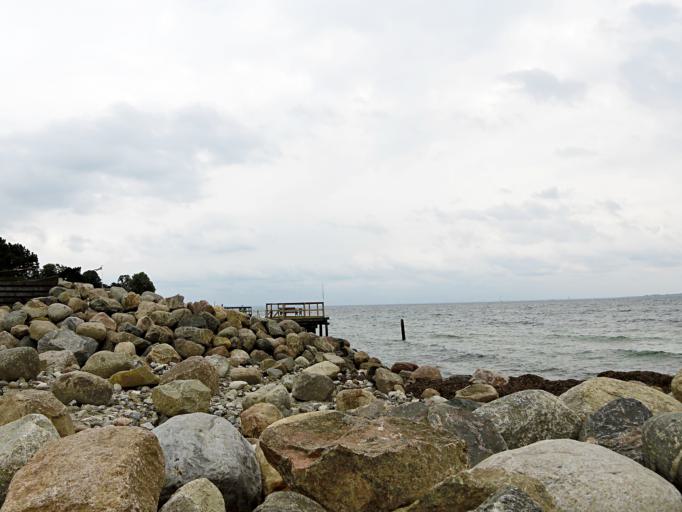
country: DK
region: Capital Region
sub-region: Rudersdal Kommune
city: Trorod
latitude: 55.8521
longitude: 12.5691
